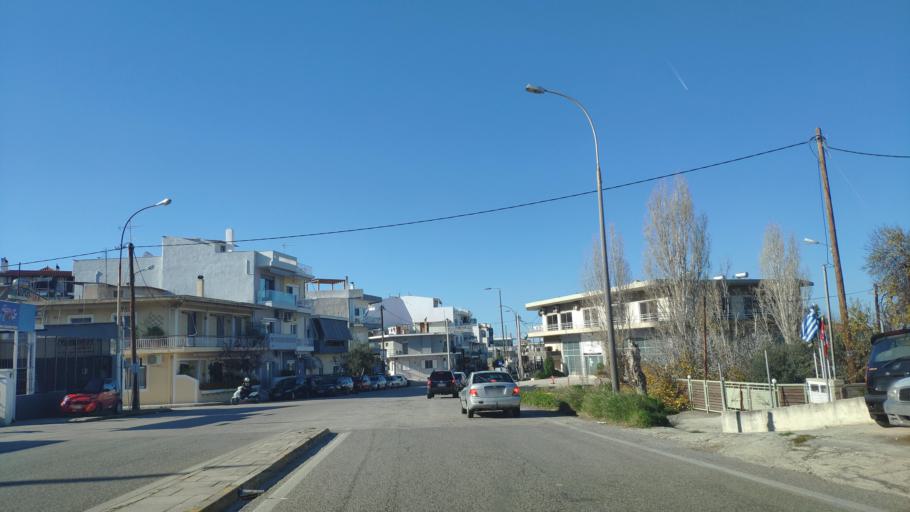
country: GR
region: Peloponnese
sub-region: Nomos Korinthias
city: Korinthos
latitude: 37.9383
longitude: 22.9517
